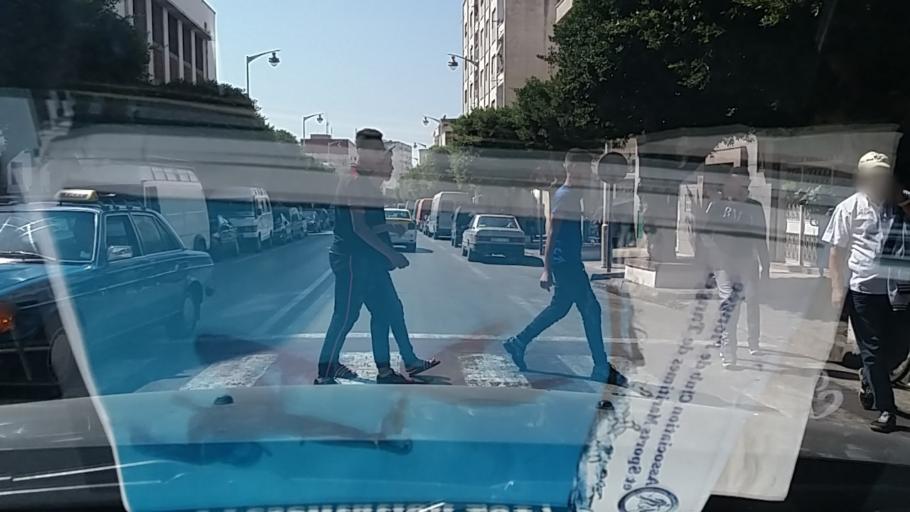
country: MA
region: Tanger-Tetouan
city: Tetouan
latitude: 35.5730
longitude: -5.3806
